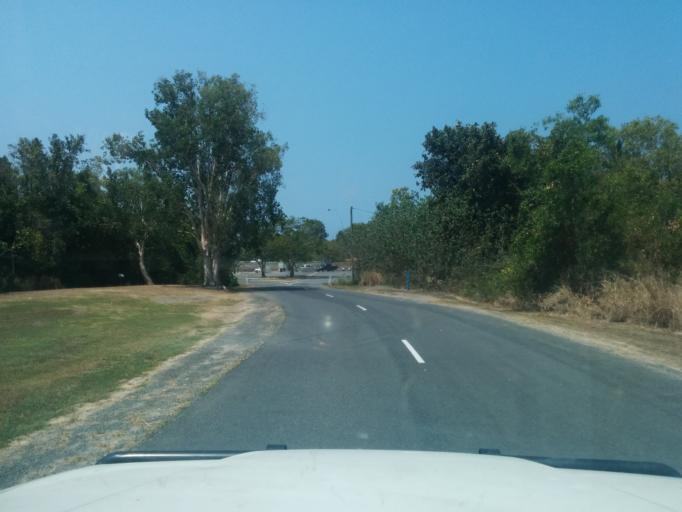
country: AU
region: Queensland
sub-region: Cairns
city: Redlynch
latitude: -16.8713
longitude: 145.7362
